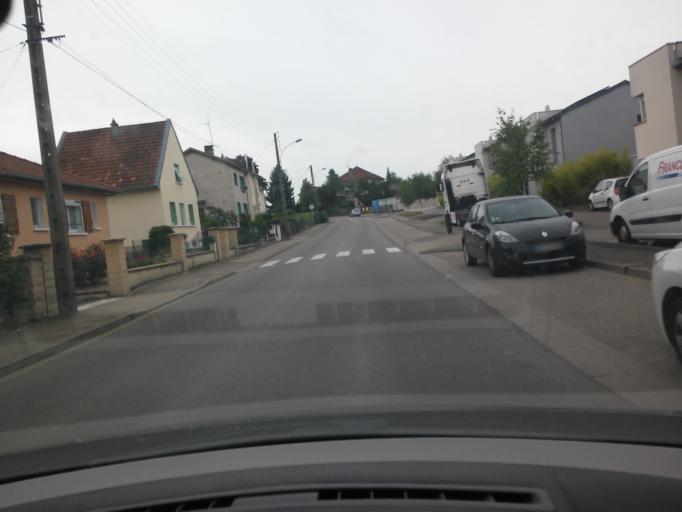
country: FR
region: Lorraine
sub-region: Departement de la Meuse
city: Commercy
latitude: 48.7630
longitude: 5.5802
